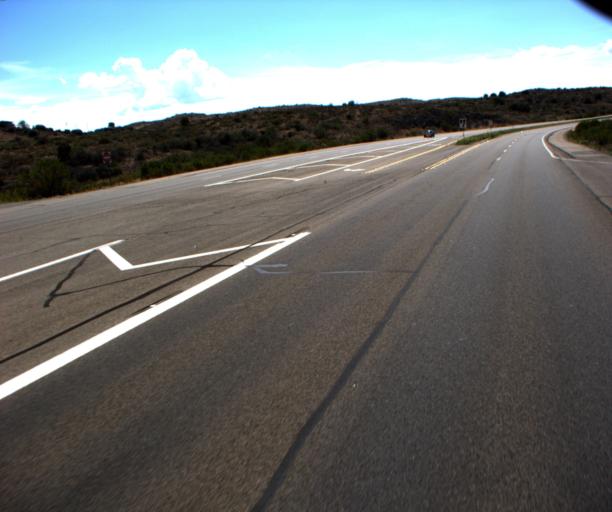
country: US
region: Arizona
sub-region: Yavapai County
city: Spring Valley
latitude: 34.3701
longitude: -112.1825
